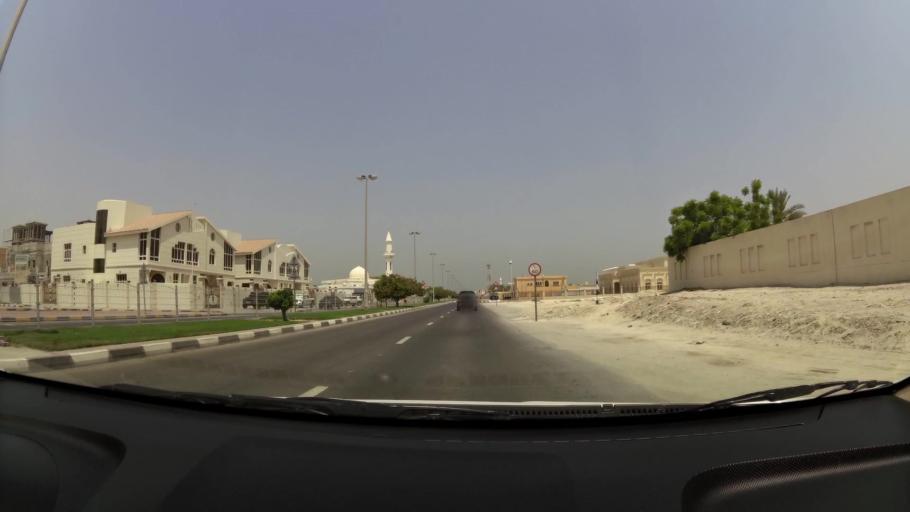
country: AE
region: Ash Shariqah
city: Sharjah
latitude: 25.3408
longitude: 55.3732
